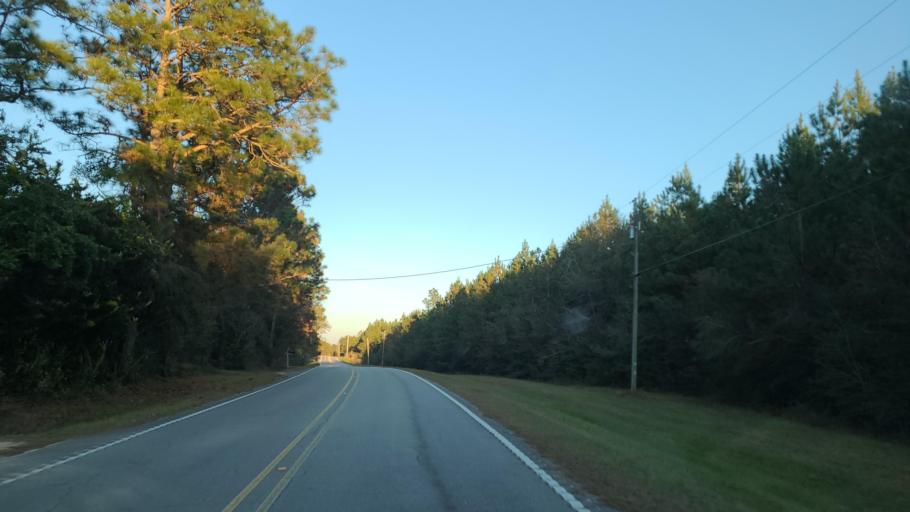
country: US
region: Mississippi
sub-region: Stone County
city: Wiggins
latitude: 31.0275
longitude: -89.2378
